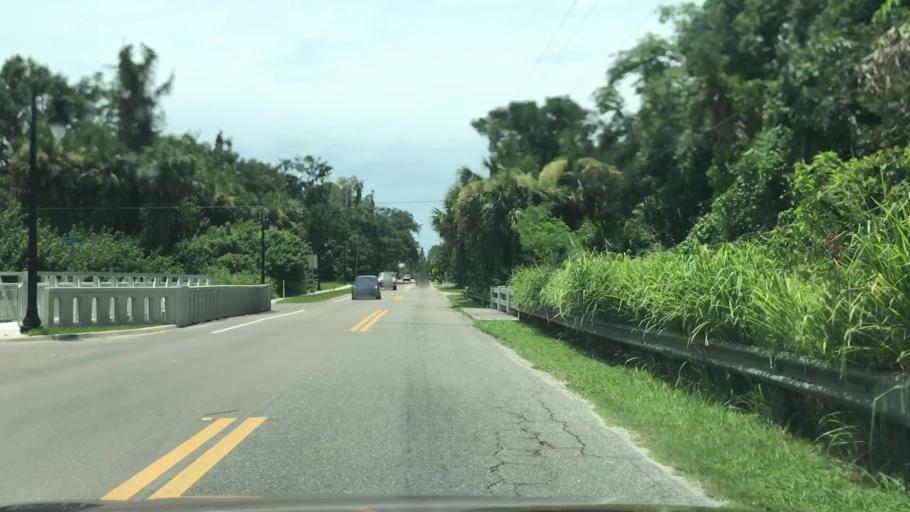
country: US
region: Florida
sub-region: Sarasota County
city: North Sarasota
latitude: 27.3672
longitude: -82.5442
